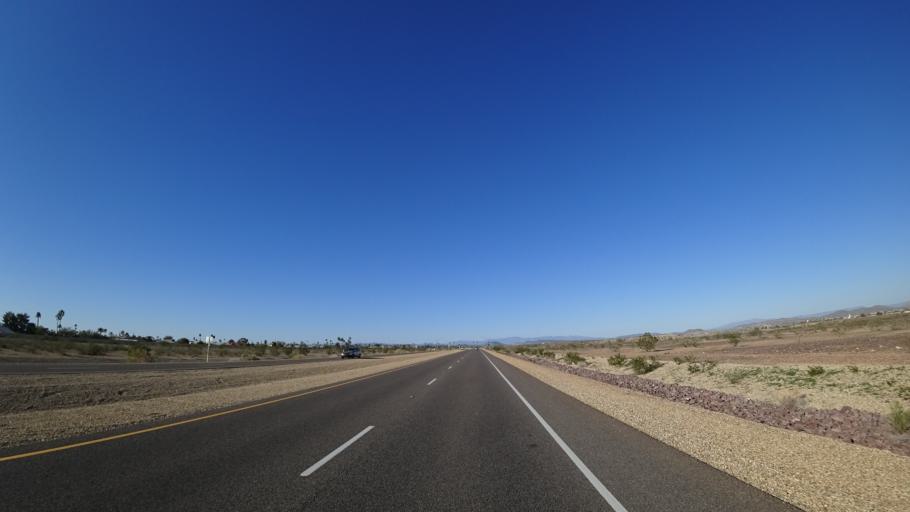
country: US
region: Arizona
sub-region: Maricopa County
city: Sun City West
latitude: 33.6537
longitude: -112.3230
